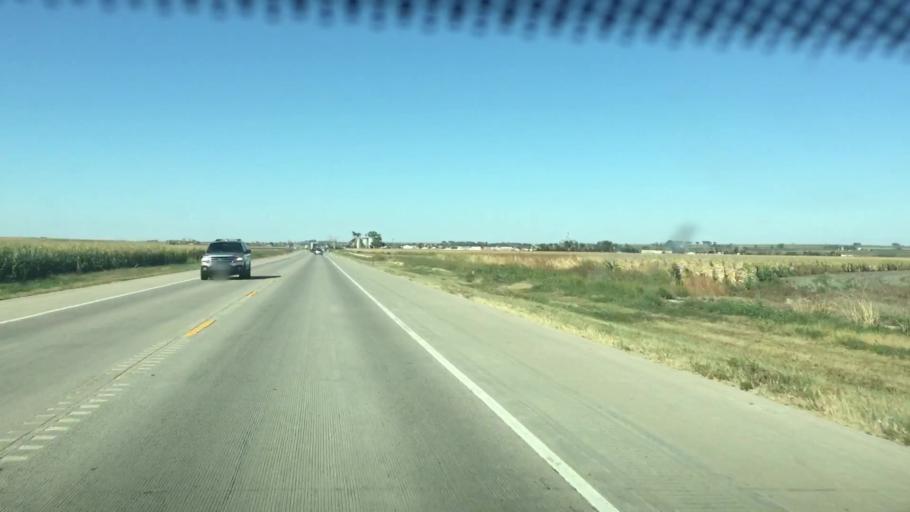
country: US
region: Colorado
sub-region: Prowers County
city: Lamar
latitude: 38.1340
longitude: -102.7236
